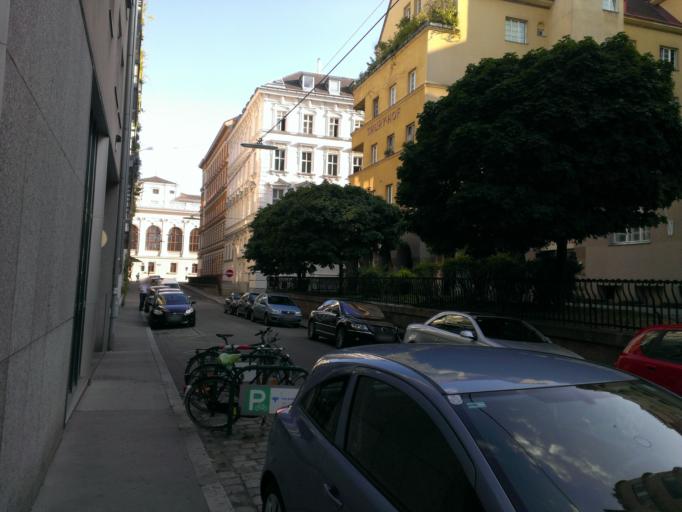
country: AT
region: Vienna
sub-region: Wien Stadt
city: Vienna
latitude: 48.2259
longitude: 16.3583
